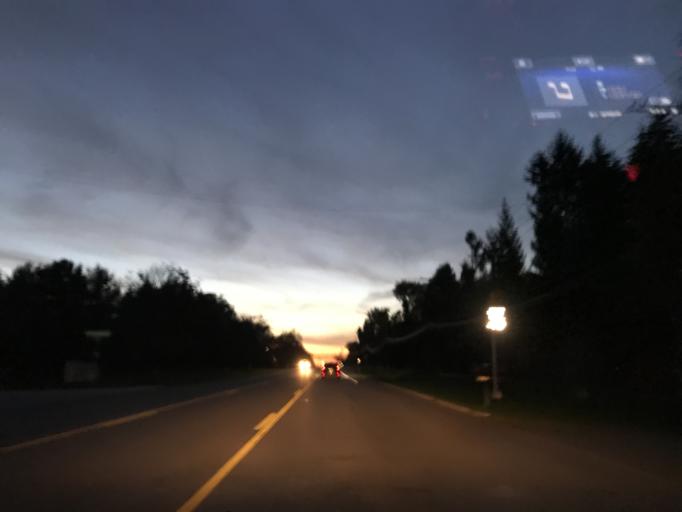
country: US
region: Michigan
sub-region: Wayne County
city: Northville
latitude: 42.4368
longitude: -83.5024
